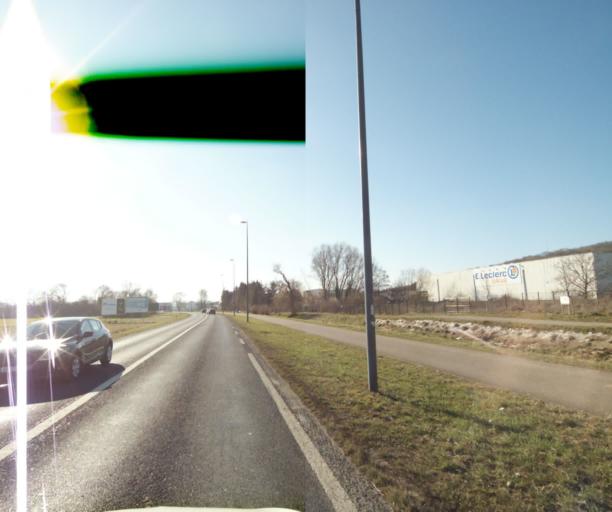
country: FR
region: Lorraine
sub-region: Departement de Meurthe-et-Moselle
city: Essey-les-Nancy
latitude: 48.7074
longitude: 6.2405
